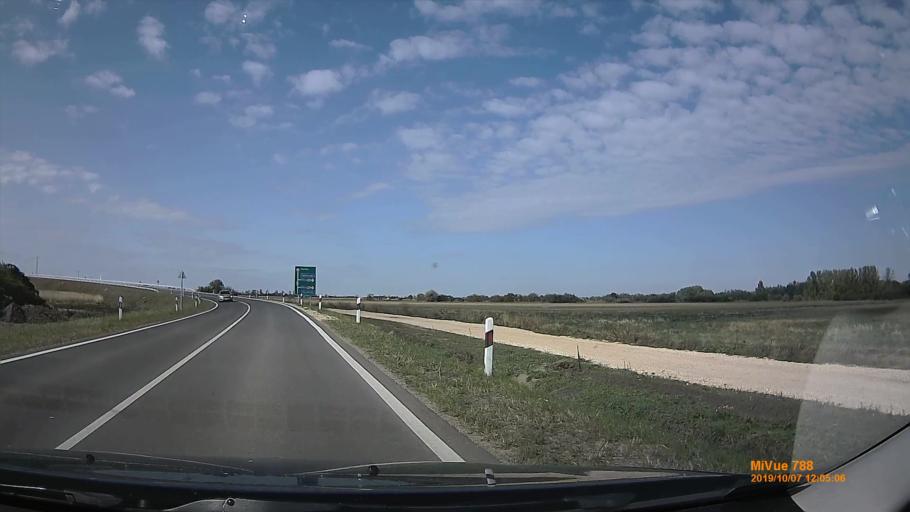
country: HU
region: Bekes
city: Szarvas
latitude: 46.8208
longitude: 20.5227
